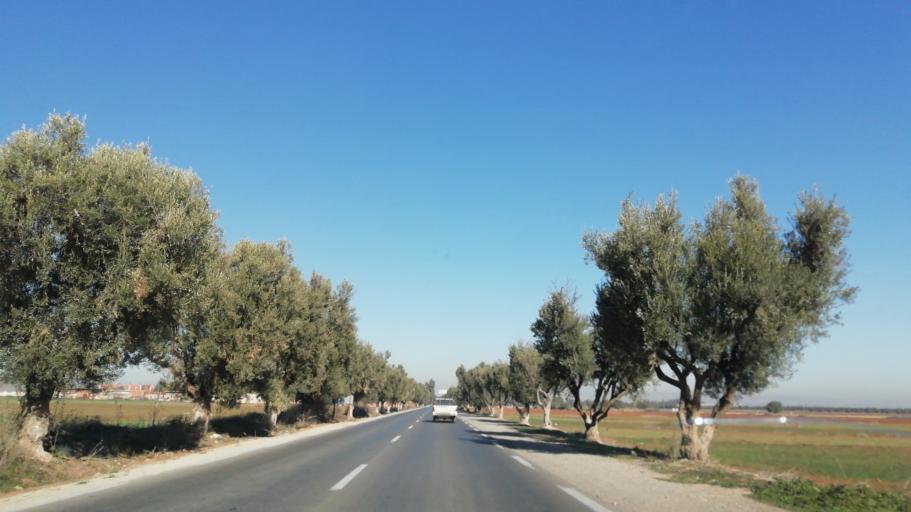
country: DZ
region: Mascara
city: Mascara
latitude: 35.2702
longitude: 0.1287
